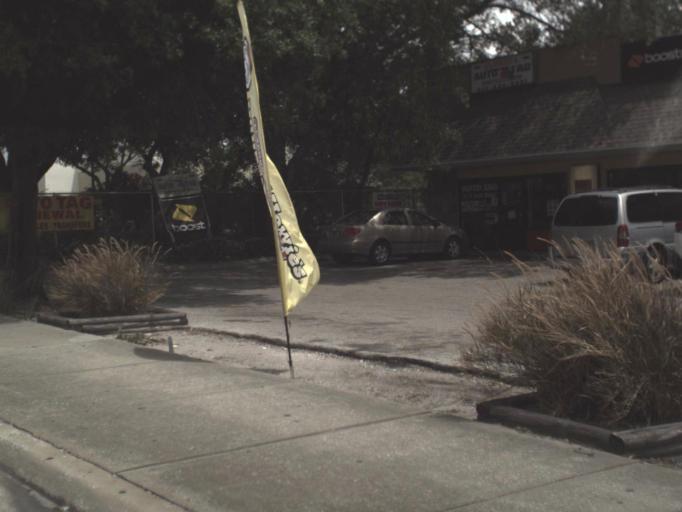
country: US
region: Florida
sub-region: Hillsborough County
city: Tampa
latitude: 27.9960
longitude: -82.4368
